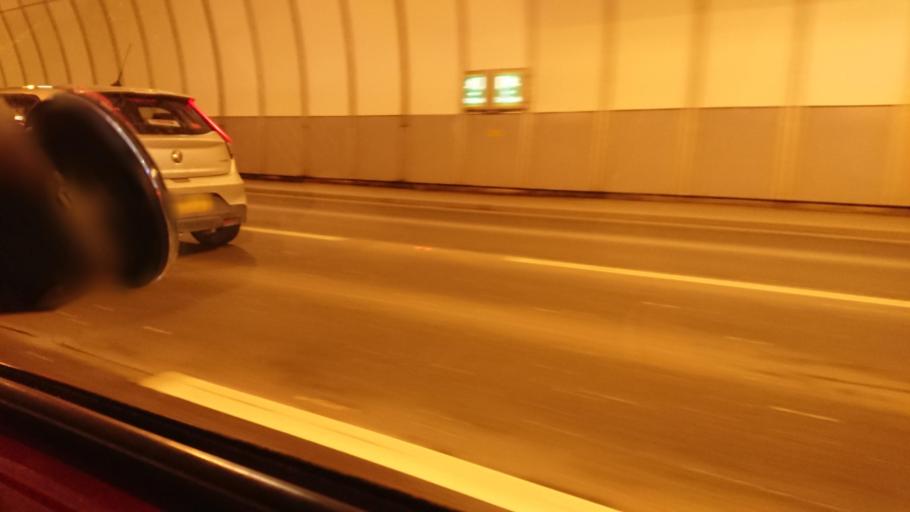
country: GB
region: England
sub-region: Cornwall
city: Saltash
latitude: 50.4106
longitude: -4.2138
